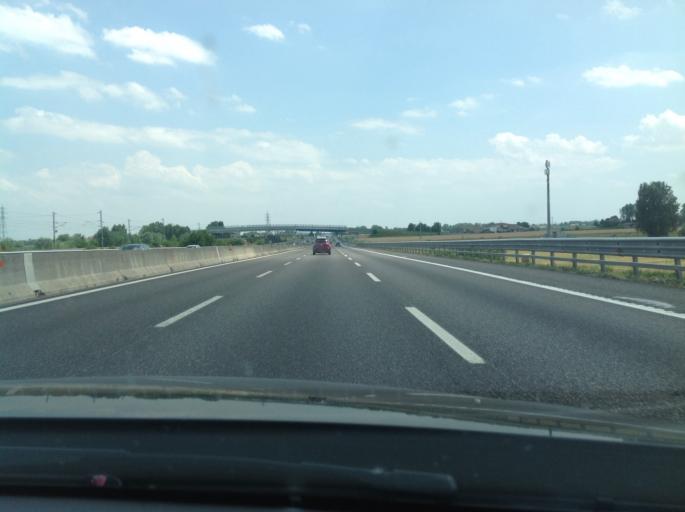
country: IT
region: Emilia-Romagna
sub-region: Provincia di Piacenza
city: Alseno
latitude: 44.9207
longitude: 9.9981
